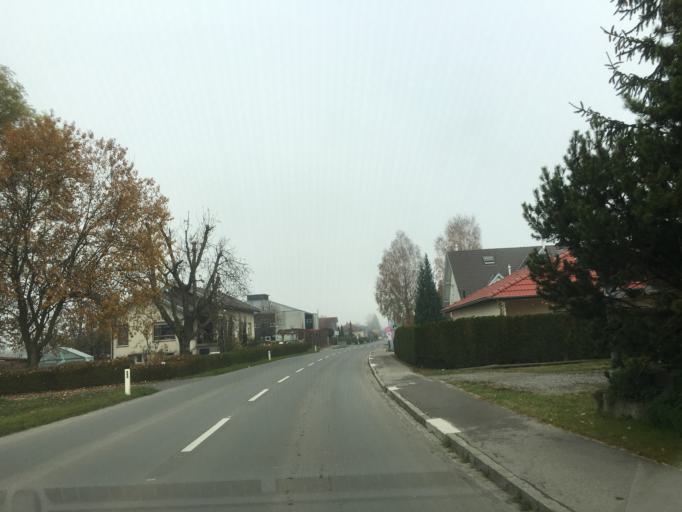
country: AT
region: Vorarlberg
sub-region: Politischer Bezirk Feldkirch
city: Koblach
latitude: 47.3208
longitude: 9.5982
